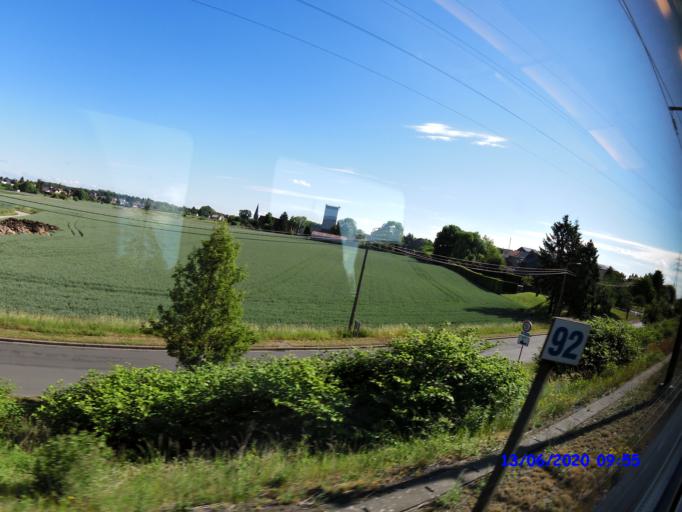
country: BE
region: Wallonia
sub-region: Province de Liege
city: Awans
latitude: 50.6584
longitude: 5.4554
